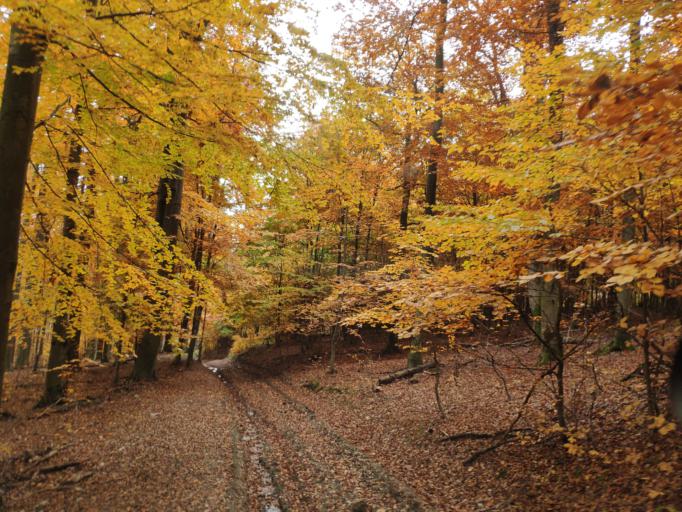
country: SK
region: Kosicky
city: Moldava nad Bodvou
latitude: 48.7336
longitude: 21.0170
